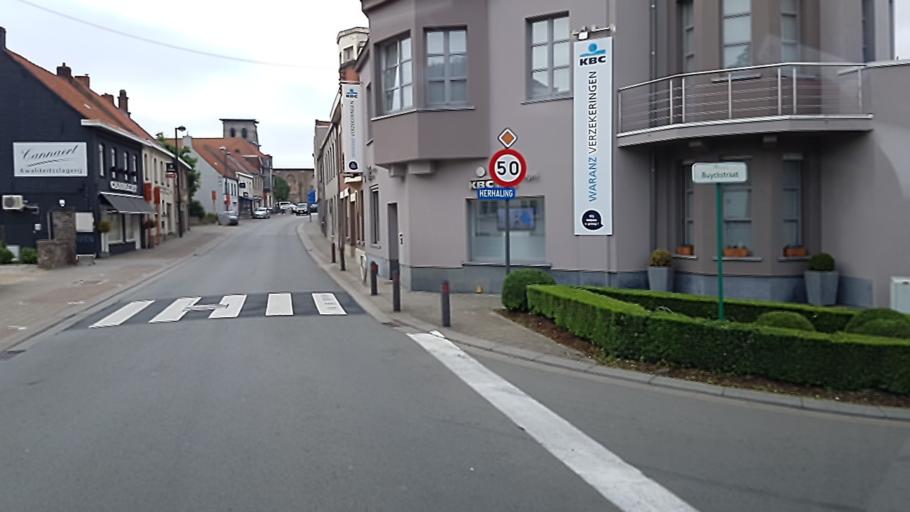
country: BE
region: Flanders
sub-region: Provincie West-Vlaanderen
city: Anzegem
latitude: 50.8338
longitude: 3.4780
